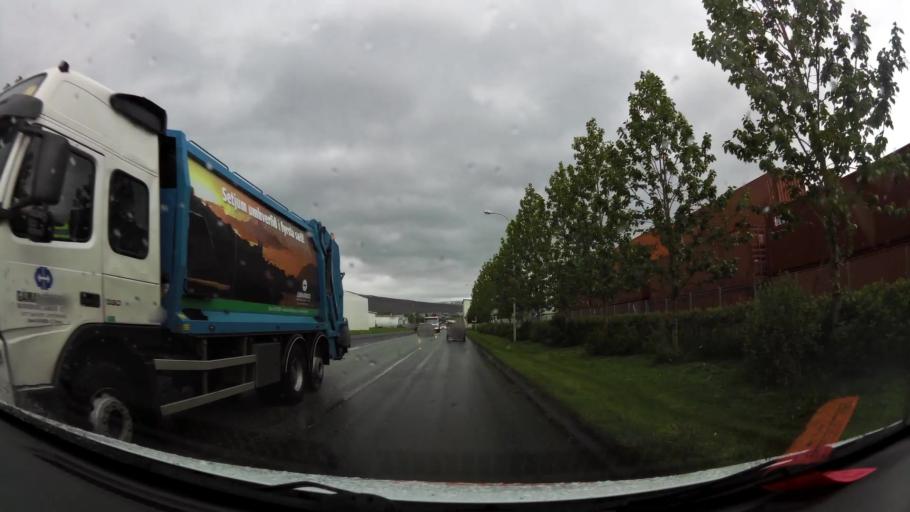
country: IS
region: Northeast
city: Akureyri
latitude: 65.6911
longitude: -18.0907
